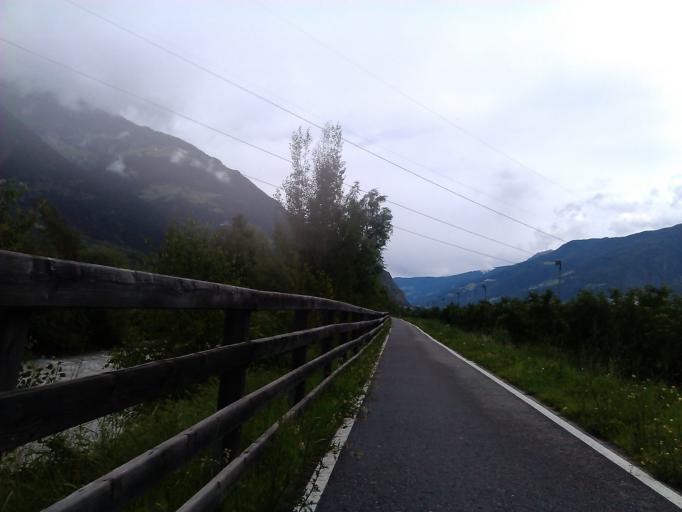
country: IT
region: Trentino-Alto Adige
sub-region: Bolzano
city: Silandro
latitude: 46.6176
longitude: 10.7962
